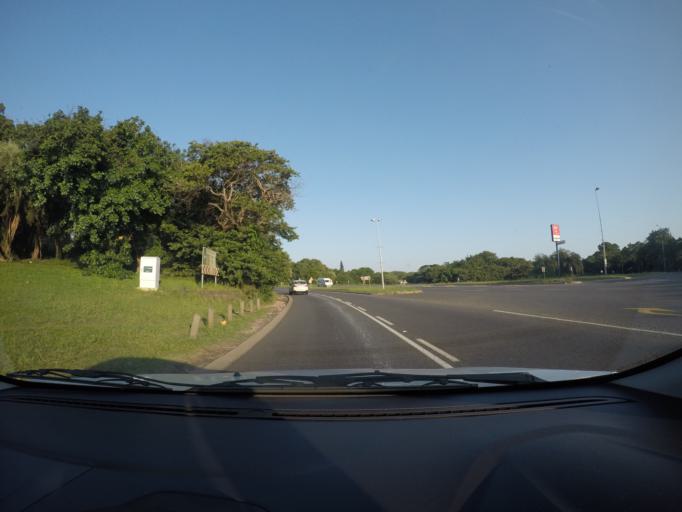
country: ZA
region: KwaZulu-Natal
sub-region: uThungulu District Municipality
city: Richards Bay
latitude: -28.7873
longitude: 32.0905
